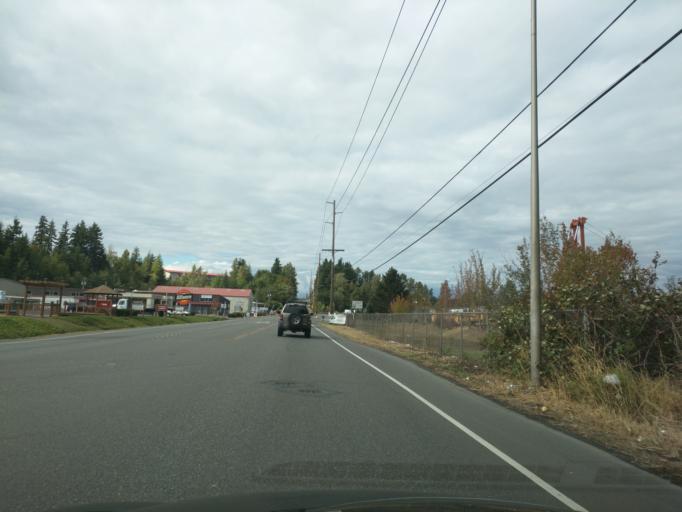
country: US
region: Washington
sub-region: Whatcom County
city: Bellingham
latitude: 48.7820
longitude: -122.4425
